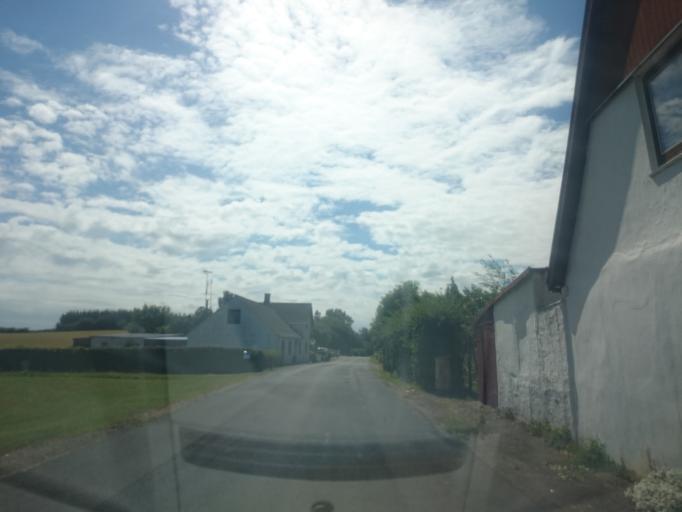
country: DK
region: South Denmark
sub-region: Langeland Kommune
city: Rudkobing
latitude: 54.9585
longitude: 10.8088
